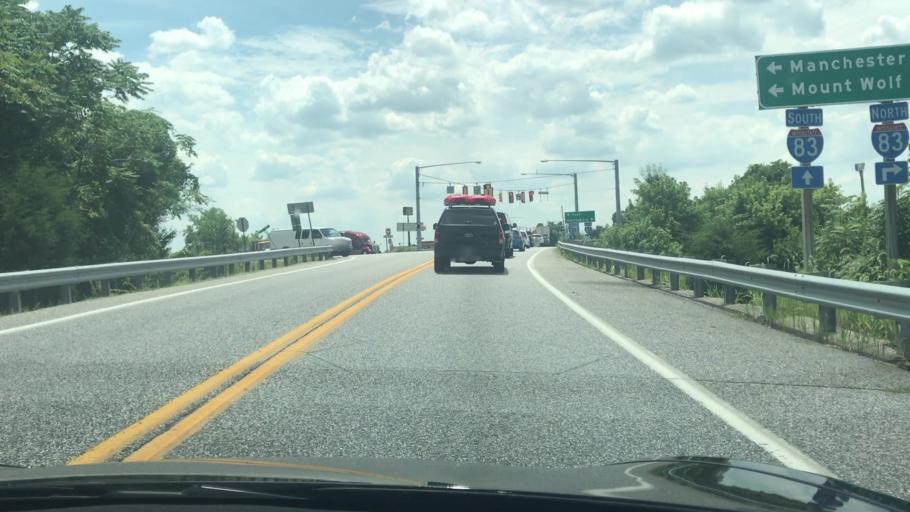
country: US
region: Pennsylvania
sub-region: York County
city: Manchester
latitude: 40.0835
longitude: -76.7641
